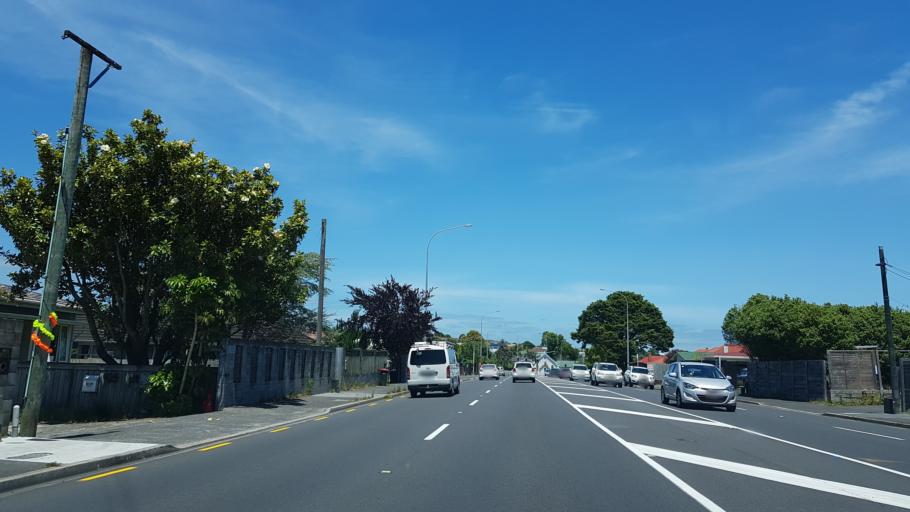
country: NZ
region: Auckland
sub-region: Auckland
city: Rosebank
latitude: -36.8846
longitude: 174.7008
